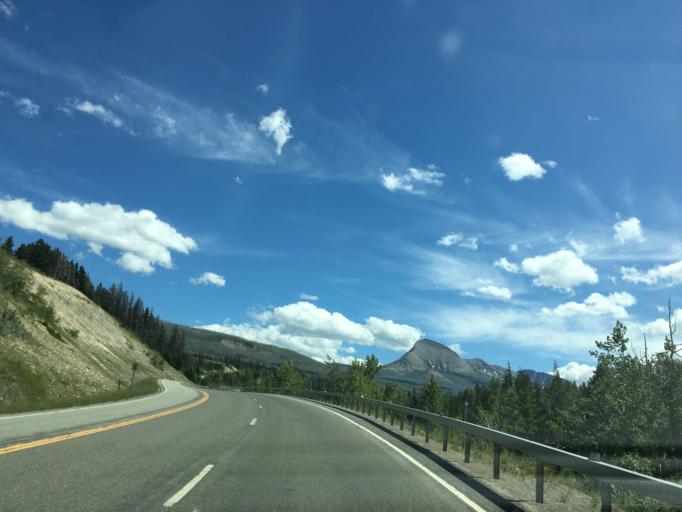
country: US
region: Montana
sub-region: Glacier County
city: North Browning
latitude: 48.7384
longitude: -113.4255
